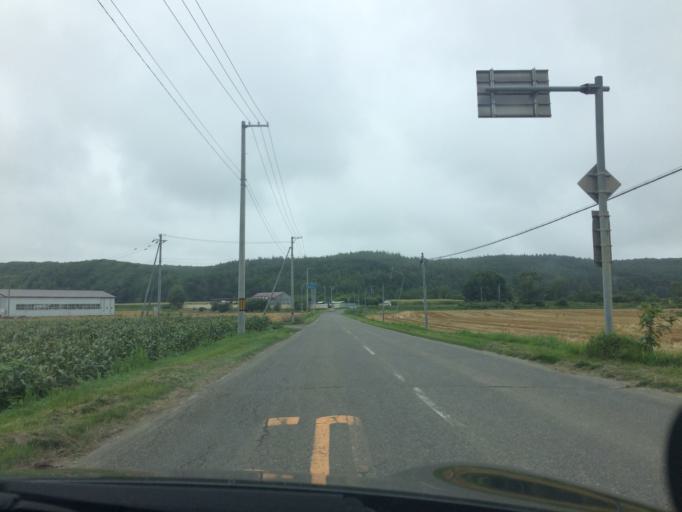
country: JP
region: Hokkaido
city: Otofuke
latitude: 42.9517
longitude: 143.1265
